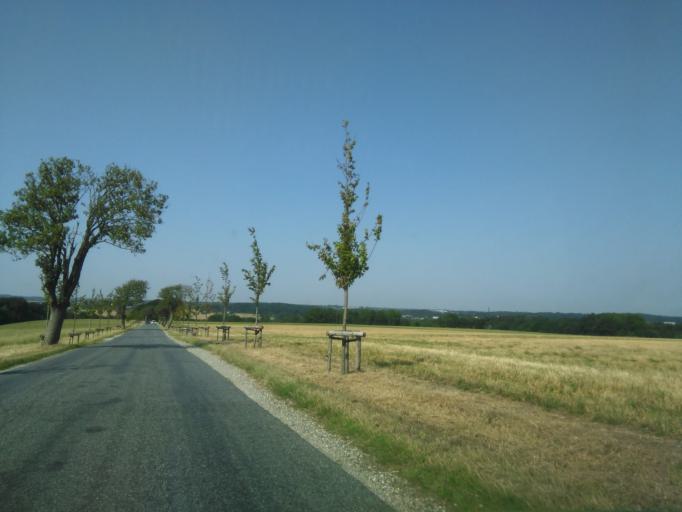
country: DK
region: Central Jutland
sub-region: Arhus Kommune
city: Kolt
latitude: 56.1317
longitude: 10.0789
